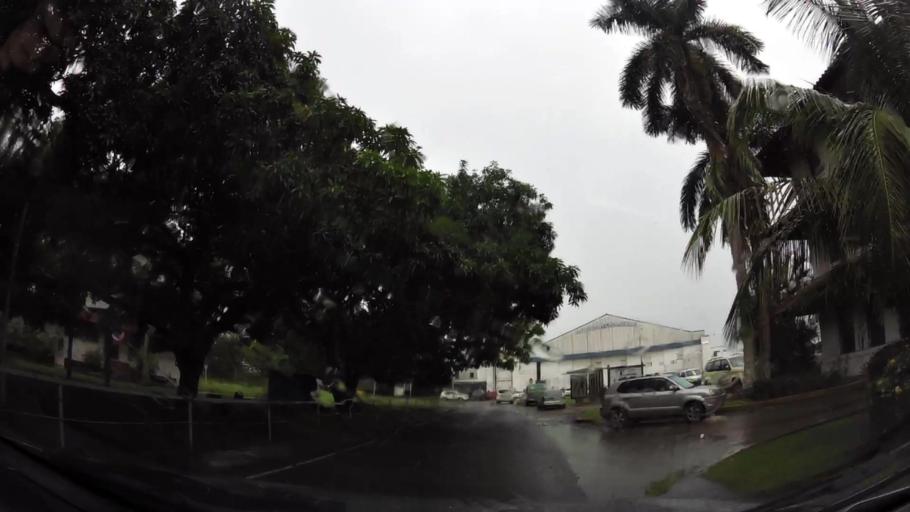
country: PA
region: Panama
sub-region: Distrito de Panama
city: Ancon
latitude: 8.9742
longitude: -79.5594
